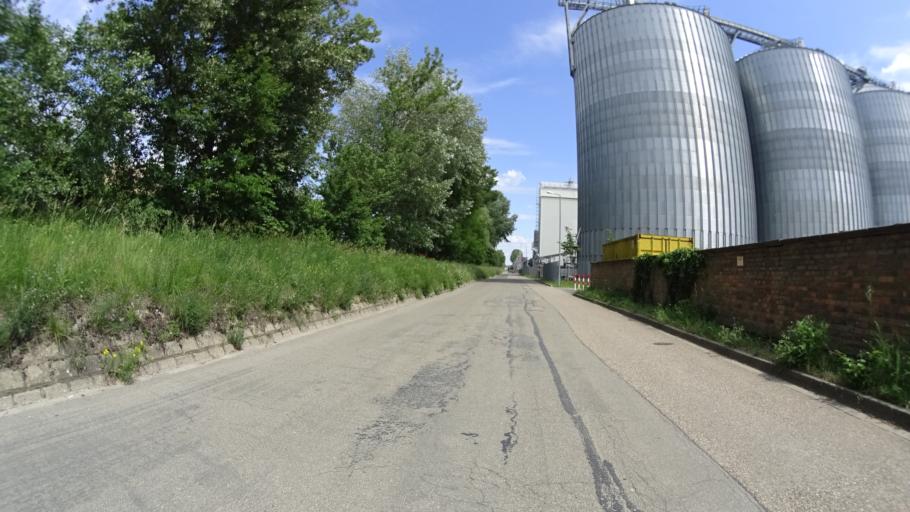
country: DE
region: Baden-Wuerttemberg
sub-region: Karlsruhe Region
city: Rheinstetten
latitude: 49.0171
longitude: 8.3165
